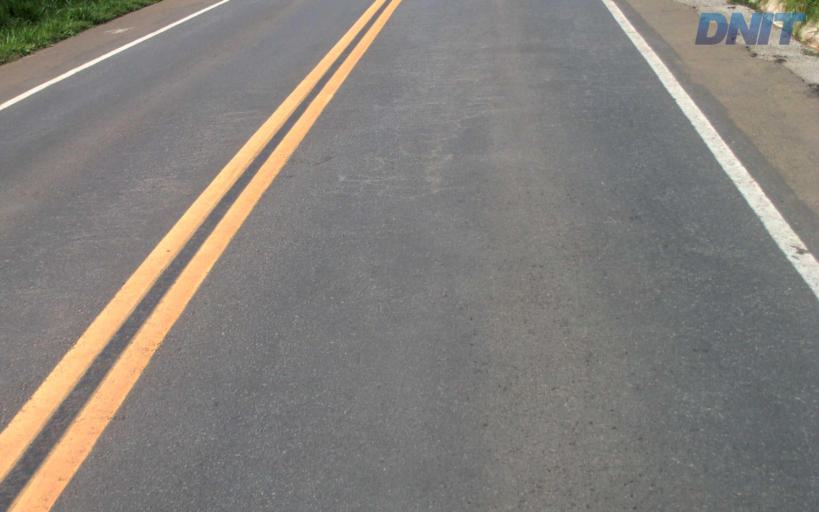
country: BR
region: Minas Gerais
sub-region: Belo Oriente
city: Belo Oriente
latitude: -19.1977
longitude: -42.2845
